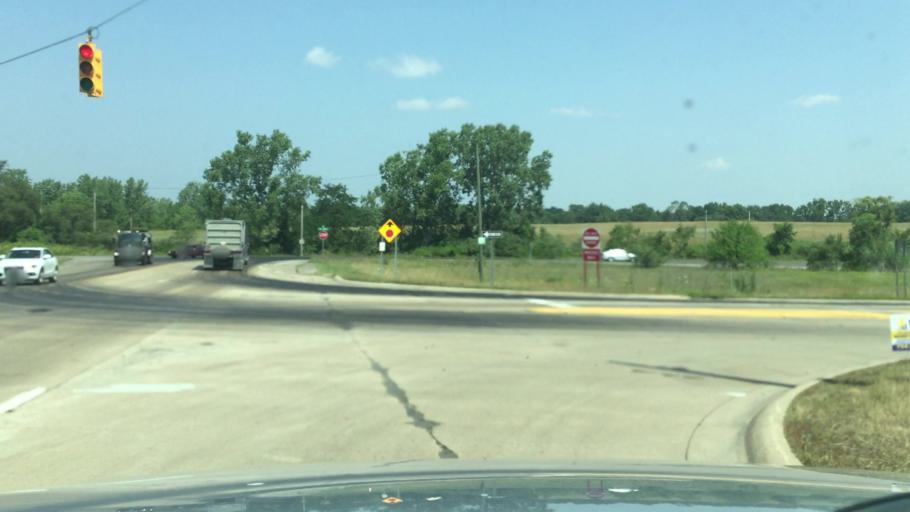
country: US
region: Michigan
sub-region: Wayne County
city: Belleville
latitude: 42.2198
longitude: -83.5465
